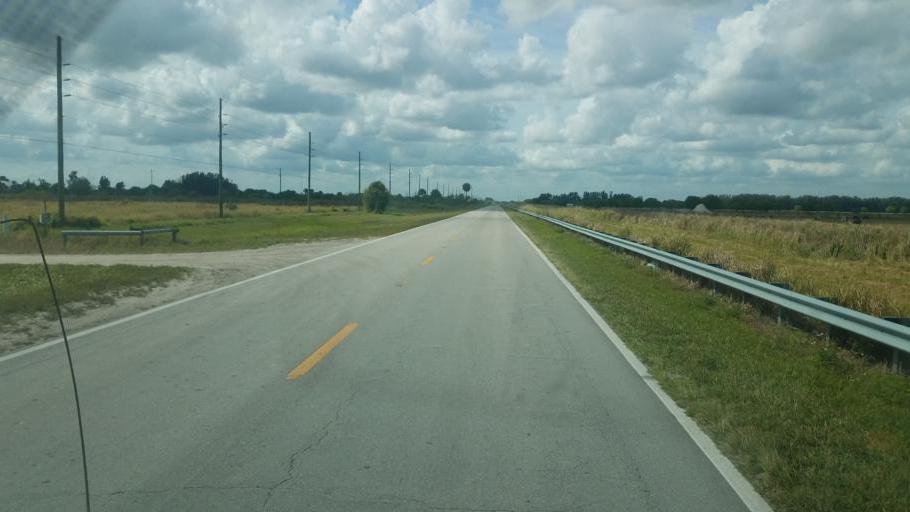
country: US
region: Florida
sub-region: Saint Lucie County
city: Lakewood Park
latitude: 27.4474
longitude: -80.5217
